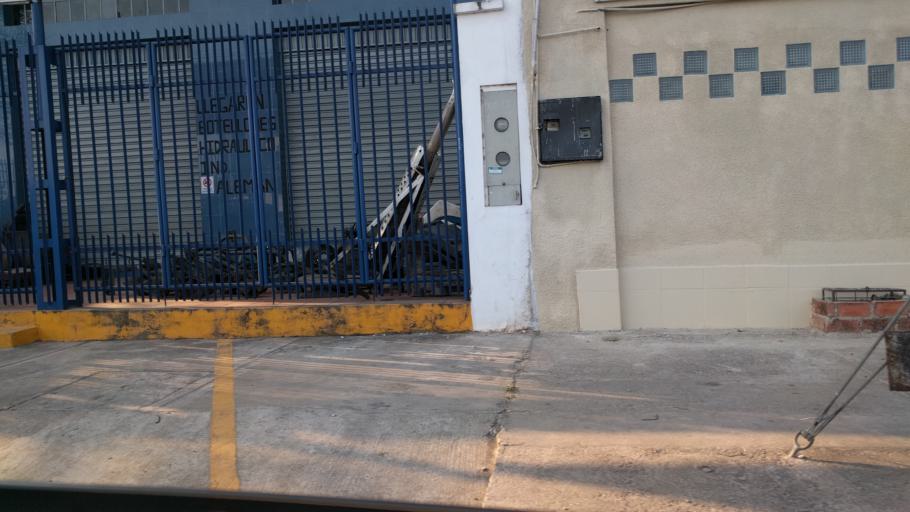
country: BO
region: Santa Cruz
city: Santa Cruz de la Sierra
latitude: -17.8056
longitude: -63.2009
